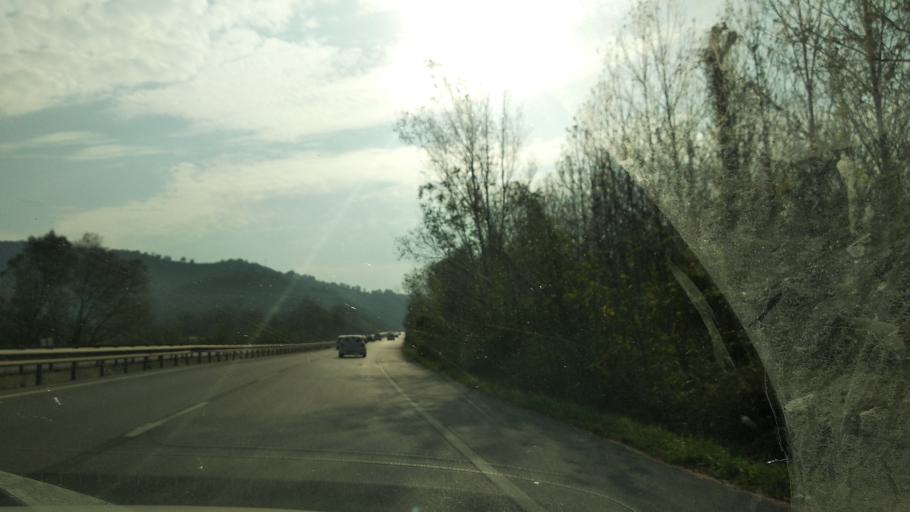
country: TR
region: Sakarya
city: Karasu
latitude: 41.0729
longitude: 30.6460
